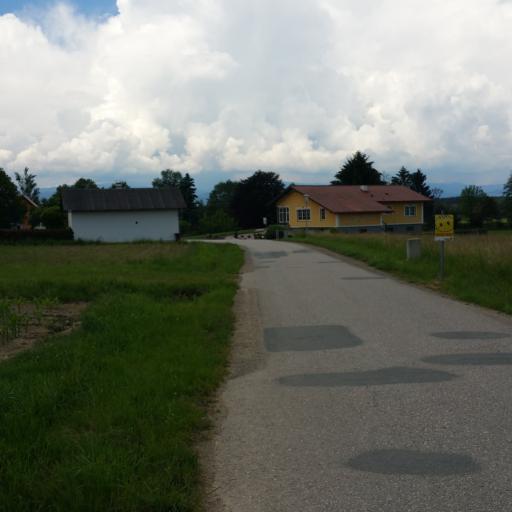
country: AT
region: Styria
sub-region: Politischer Bezirk Leibnitz
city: Gleinstatten
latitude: 46.7488
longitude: 15.3827
